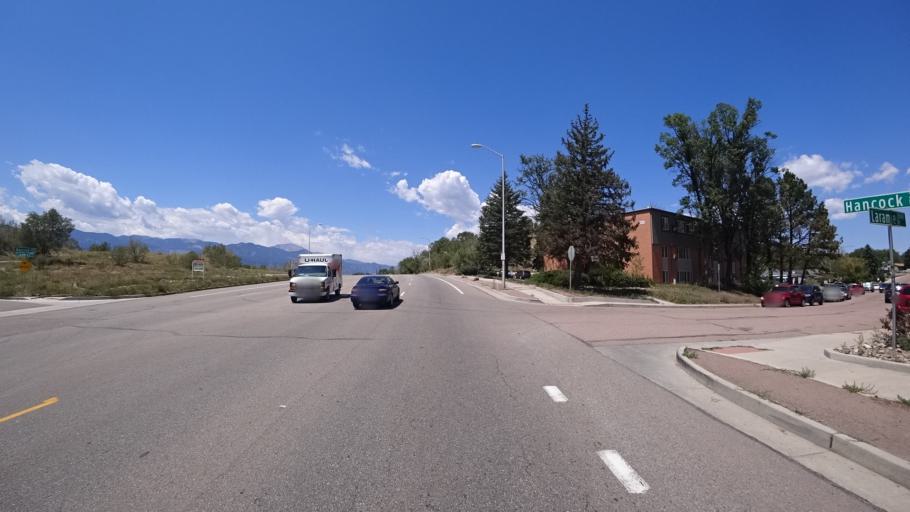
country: US
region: Colorado
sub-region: El Paso County
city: Stratmoor
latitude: 38.7956
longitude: -104.7699
